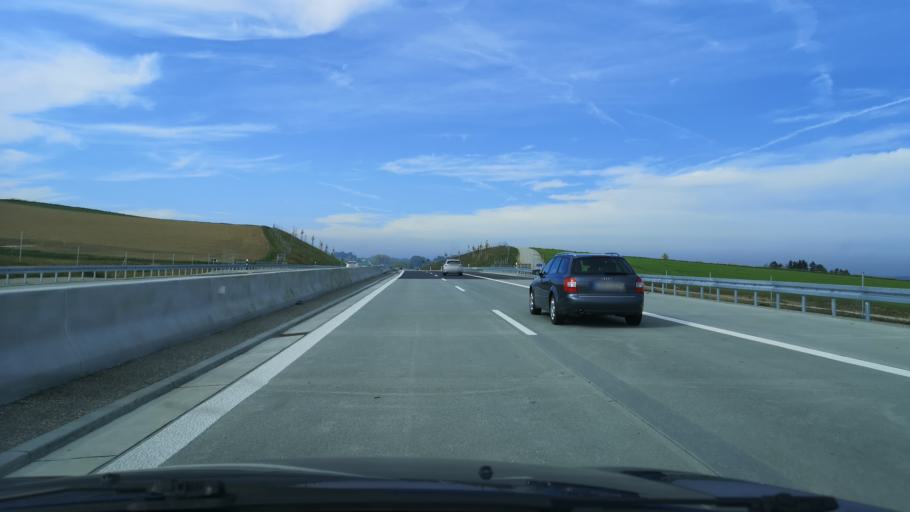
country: DE
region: Bavaria
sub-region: Upper Bavaria
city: Rattenkirchen
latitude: 48.2508
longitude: 12.3259
